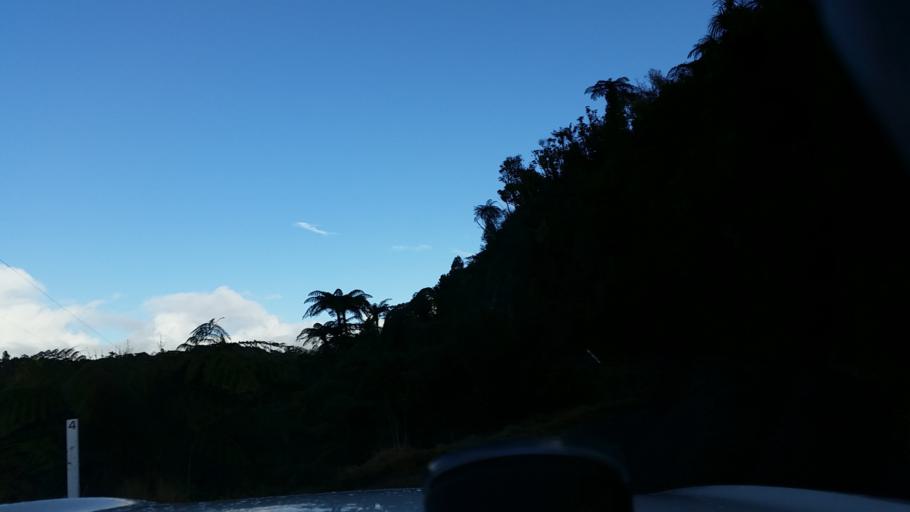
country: NZ
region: Taranaki
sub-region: South Taranaki District
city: Eltham
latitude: -39.4168
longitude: 174.5598
